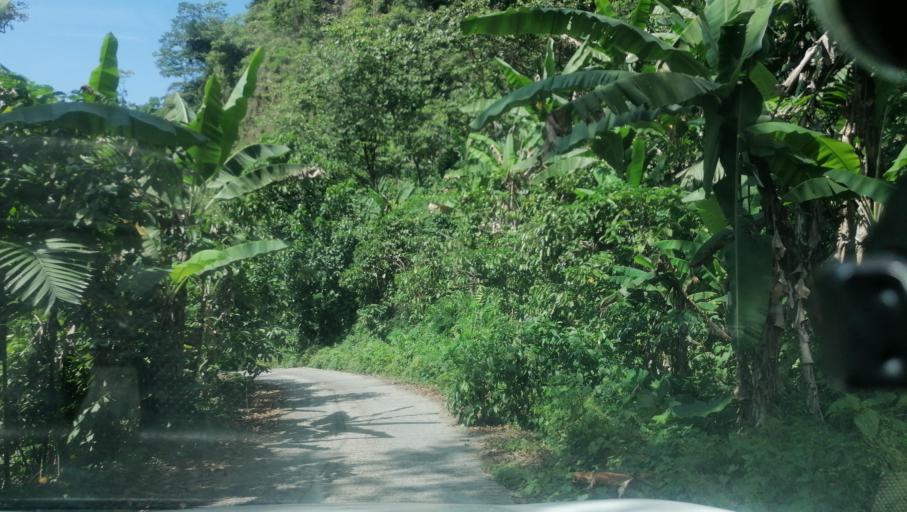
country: MX
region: Chiapas
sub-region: Union Juarez
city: Santo Domingo
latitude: 15.0720
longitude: -92.1313
